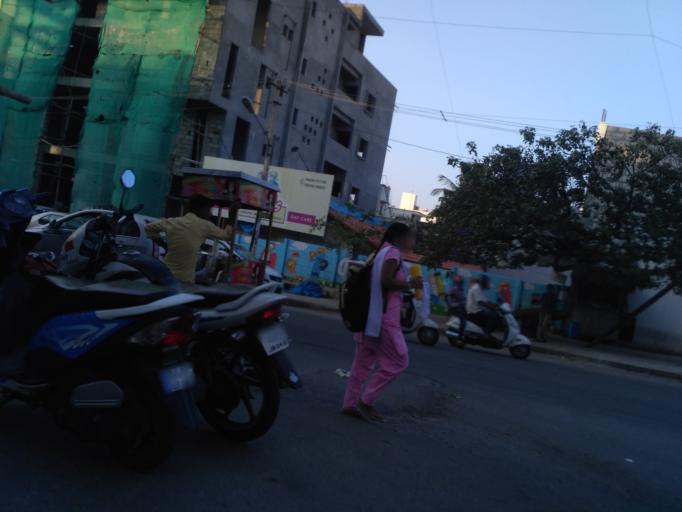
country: IN
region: Karnataka
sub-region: Bangalore Urban
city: Bangalore
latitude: 12.9606
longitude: 77.5292
